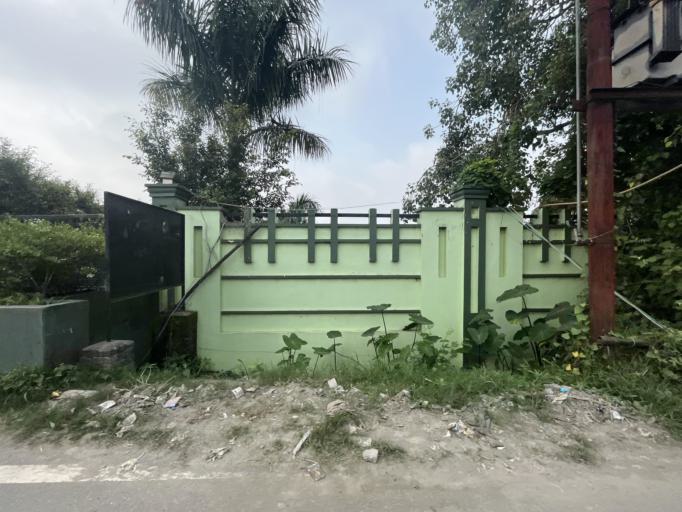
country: IN
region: Uttarakhand
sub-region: Naini Tal
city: Haldwani
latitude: 29.1942
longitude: 79.5052
